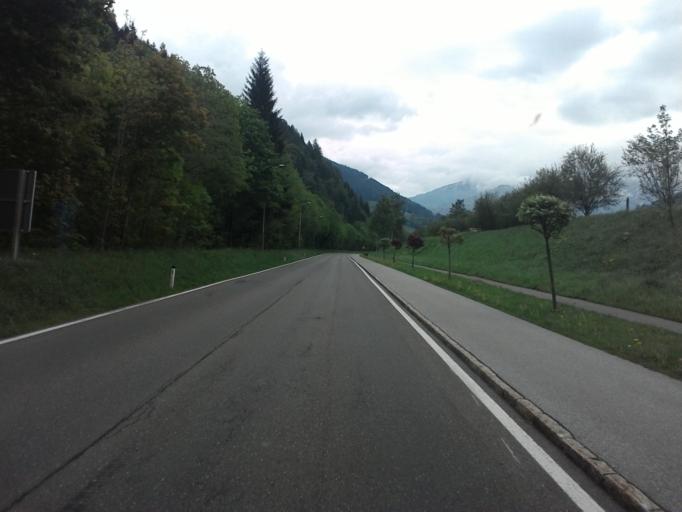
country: AT
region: Styria
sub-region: Politischer Bezirk Leoben
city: Eisenerz
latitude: 47.5648
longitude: 14.8573
